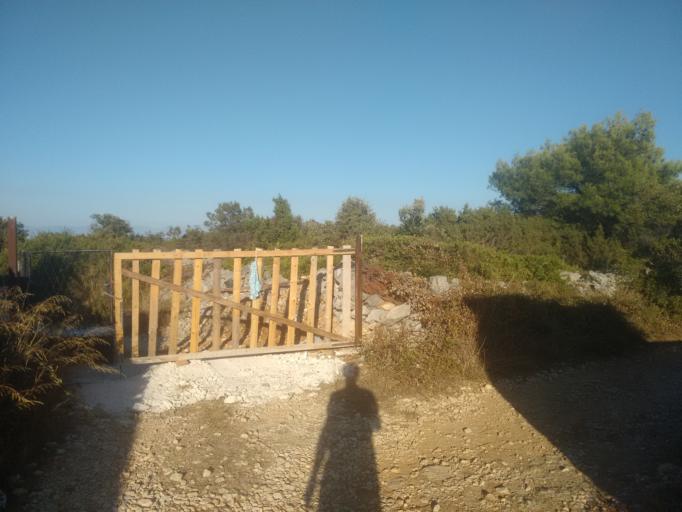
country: HR
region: Licko-Senjska
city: Novalja
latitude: 44.3711
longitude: 14.6981
